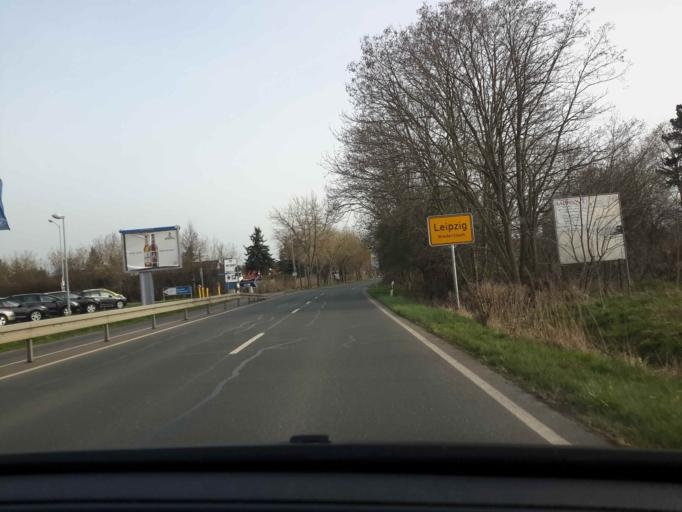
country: DE
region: Saxony
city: Rackwitz
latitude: 51.4044
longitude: 12.3666
